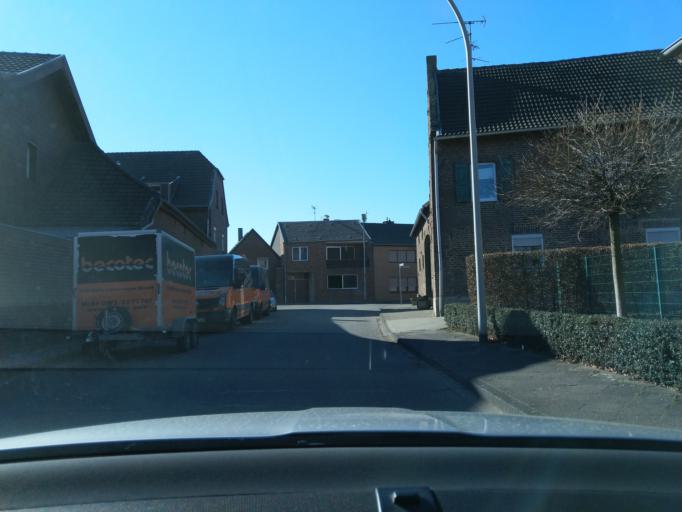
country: DE
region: North Rhine-Westphalia
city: Erkelenz
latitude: 51.1088
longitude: 6.3842
